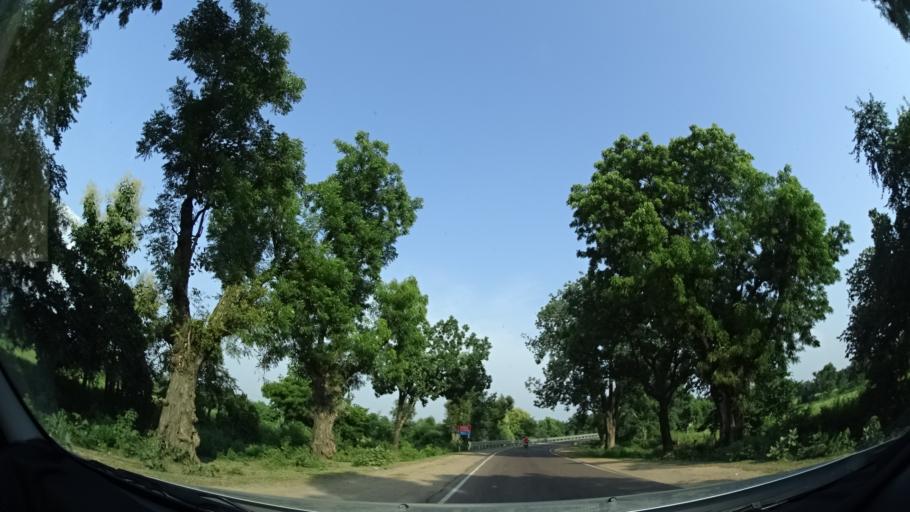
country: IN
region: Madhya Pradesh
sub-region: Chhatarpur
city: Khajuraho
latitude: 24.7837
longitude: 79.8001
